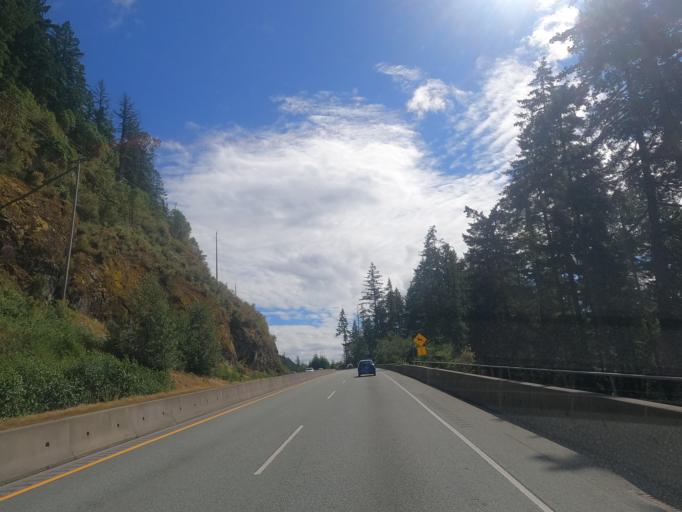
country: CA
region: British Columbia
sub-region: Greater Vancouver Regional District
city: Bowen Island
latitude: 49.3787
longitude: -123.2660
